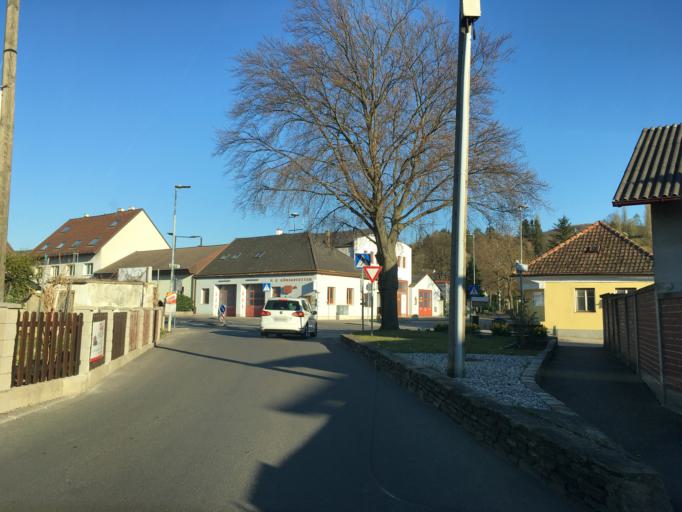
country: AT
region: Lower Austria
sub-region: Politischer Bezirk Tulln
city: Konigstetten
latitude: 48.3035
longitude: 16.1505
